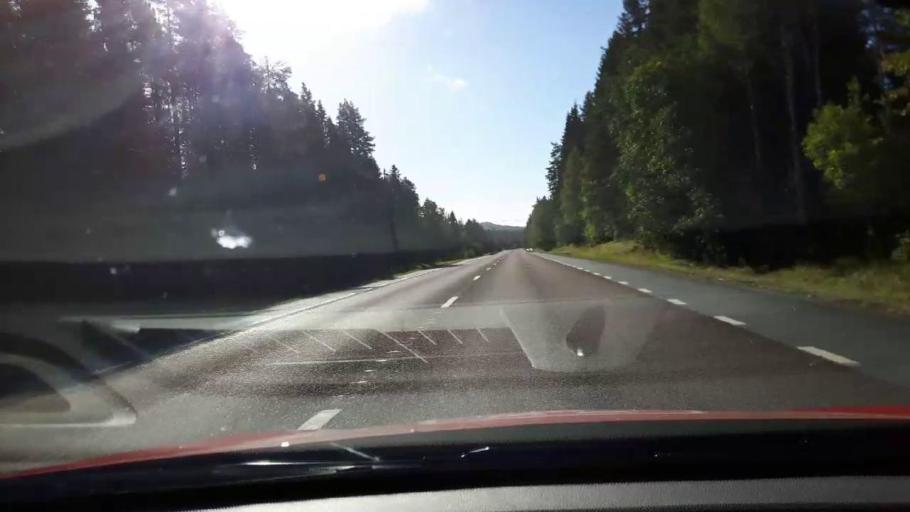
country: SE
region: Jaemtland
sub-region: Braecke Kommun
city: Braecke
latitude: 62.8812
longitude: 15.2904
